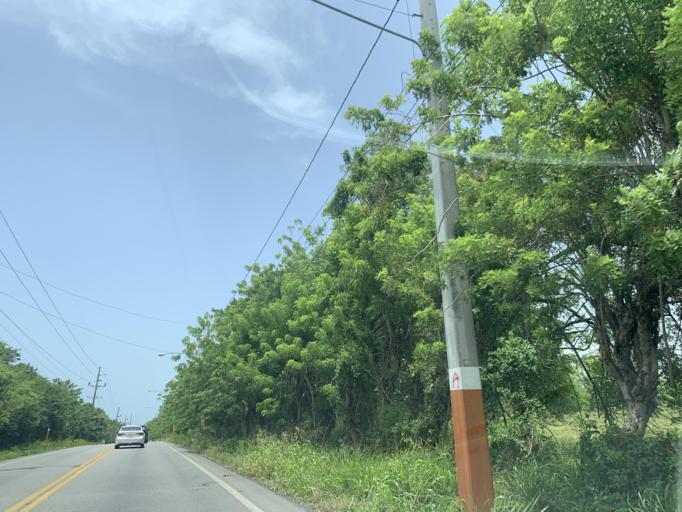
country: DO
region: Puerto Plata
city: Cabarete
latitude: 19.7779
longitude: -70.4745
